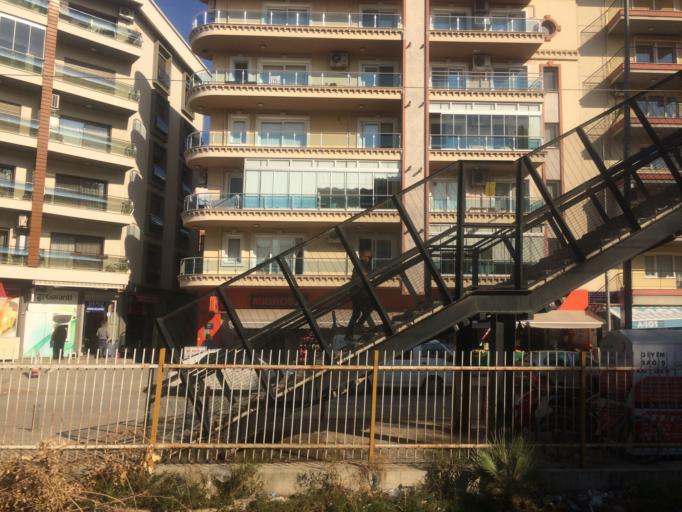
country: TR
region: Izmir
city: Karsiyaka
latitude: 38.4707
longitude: 27.0941
